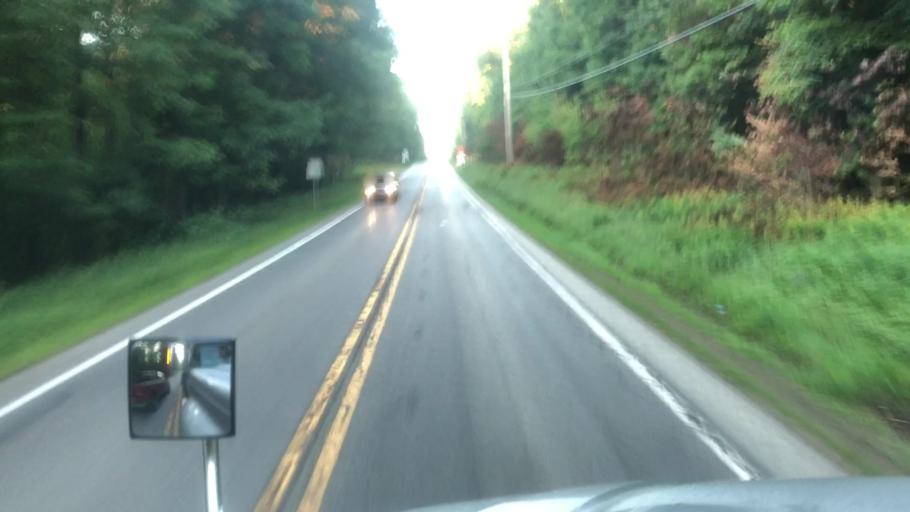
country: US
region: Pennsylvania
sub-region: Venango County
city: Hasson Heights
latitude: 41.5186
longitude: -79.6184
